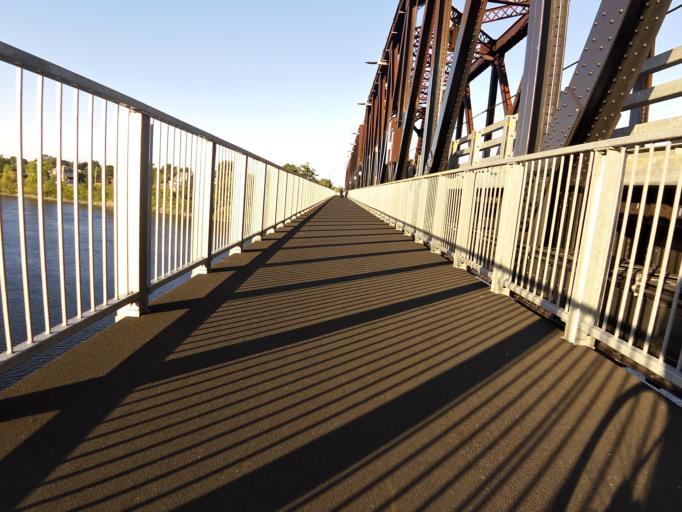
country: CA
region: Quebec
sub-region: Outaouais
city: Gatineau
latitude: 45.4632
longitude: -75.7252
